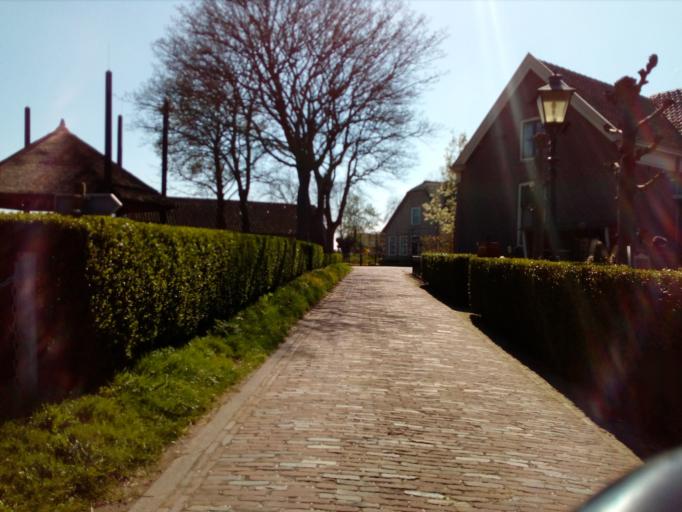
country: NL
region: South Holland
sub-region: Gemeente Westland
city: Kwintsheul
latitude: 51.9957
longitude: 4.2938
